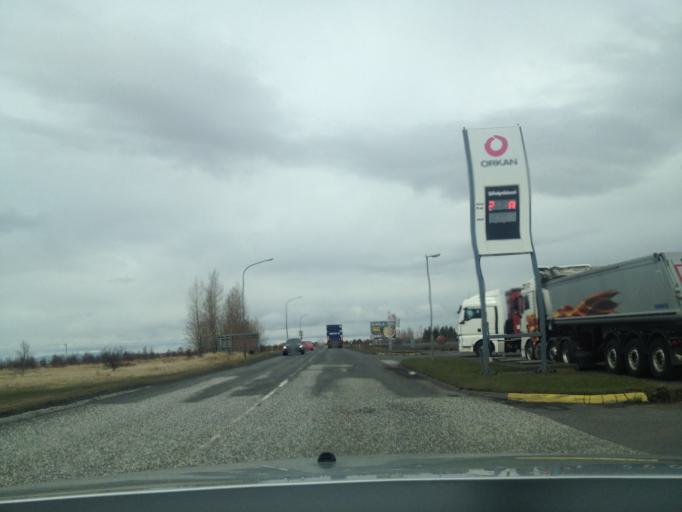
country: IS
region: South
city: Vestmannaeyjar
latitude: 63.7515
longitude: -20.2357
